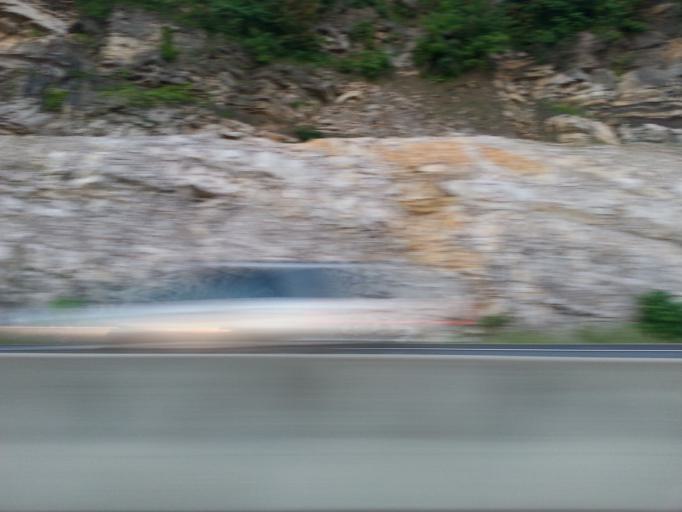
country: US
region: Tennessee
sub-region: Campbell County
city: Jellico
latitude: 36.5567
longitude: -84.1321
